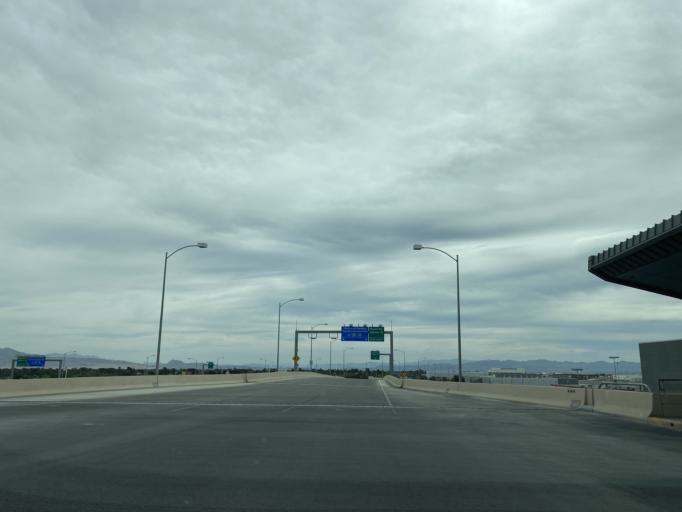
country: US
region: Nevada
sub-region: Clark County
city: Paradise
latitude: 36.0868
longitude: -115.1348
